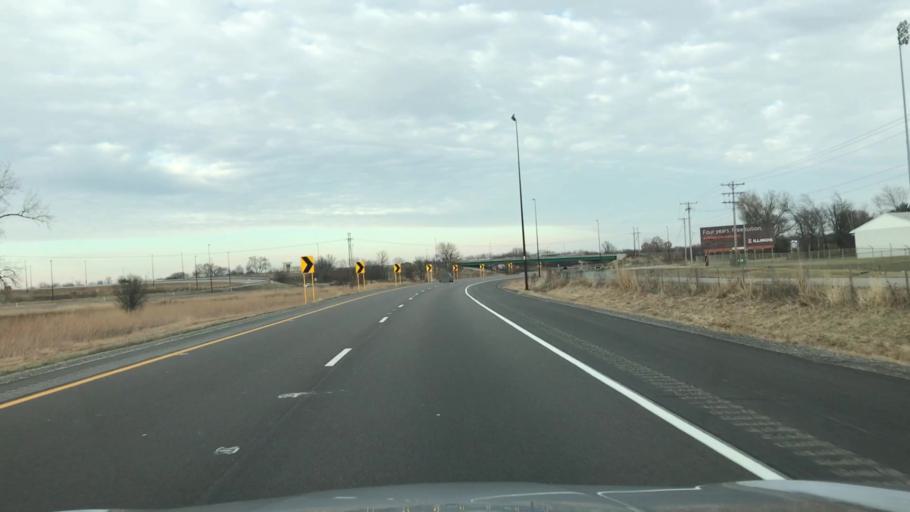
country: US
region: Illinois
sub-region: Sangamon County
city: Southern View
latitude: 39.7388
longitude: -89.6426
